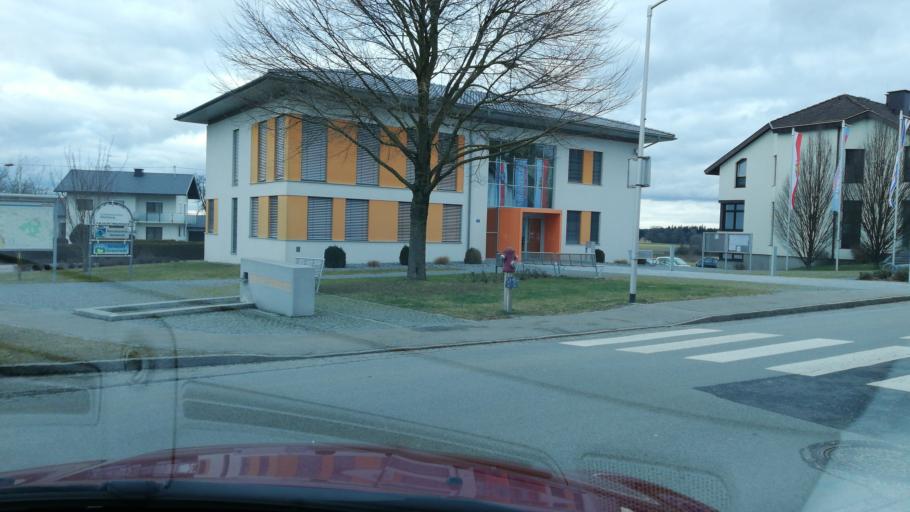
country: AT
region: Upper Austria
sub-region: Politischer Bezirk Braunau am Inn
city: Altheim
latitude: 48.2644
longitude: 13.2929
